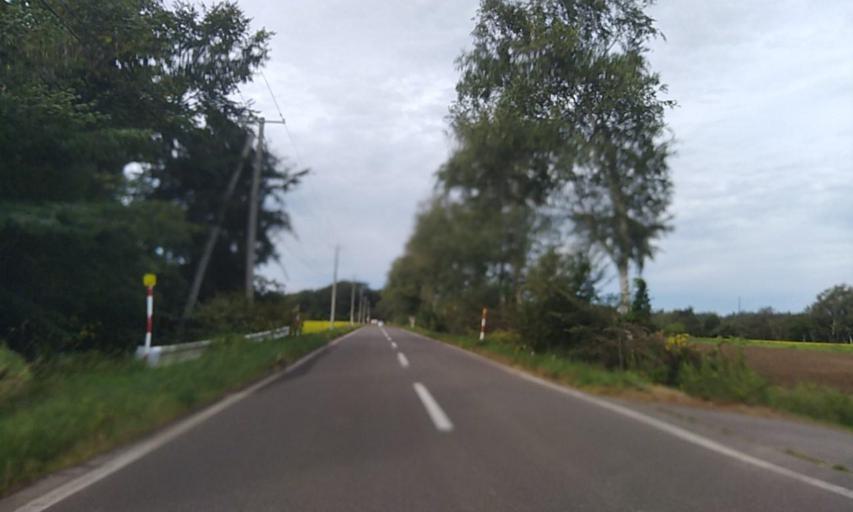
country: JP
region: Hokkaido
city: Abashiri
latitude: 43.7956
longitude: 144.5545
